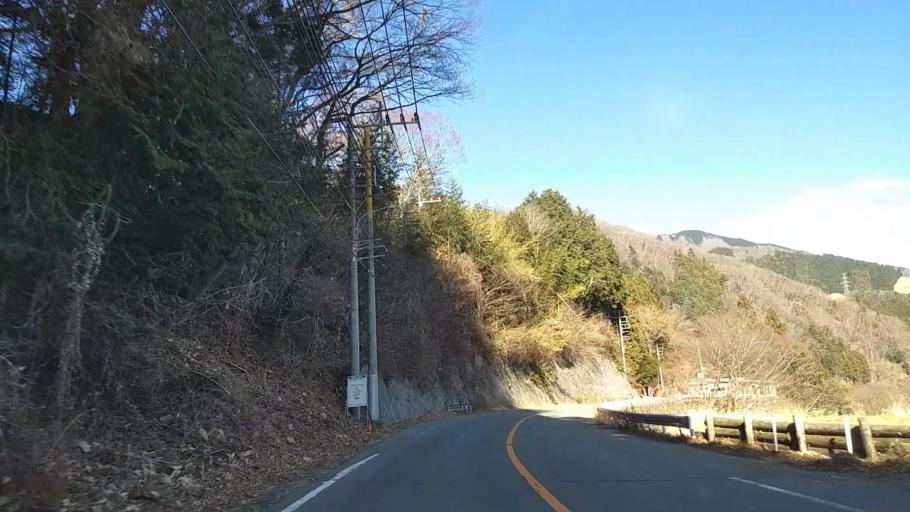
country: JP
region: Yamanashi
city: Otsuki
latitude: 35.5240
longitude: 139.0243
